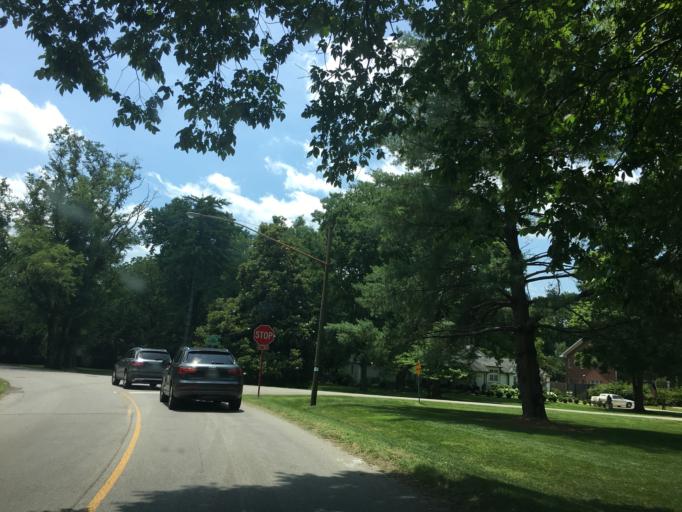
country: US
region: Tennessee
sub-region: Davidson County
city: Belle Meade
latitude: 36.1122
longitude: -86.8257
